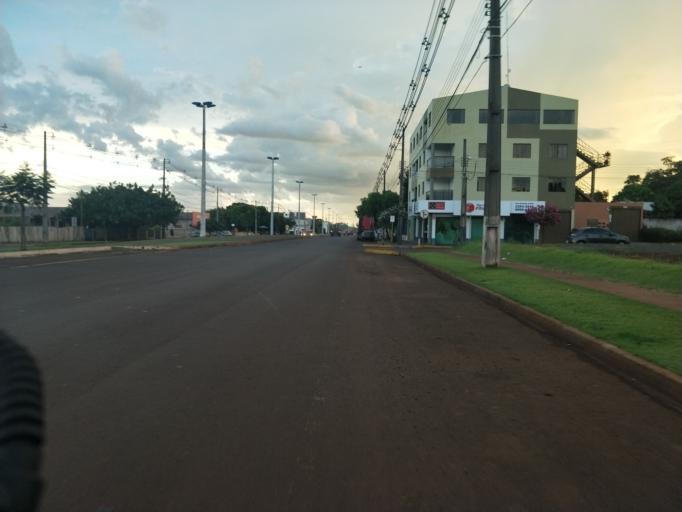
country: BR
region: Parana
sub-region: Marechal Candido Rondon
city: Marechal Candido Rondon
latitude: -24.5504
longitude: -54.0458
